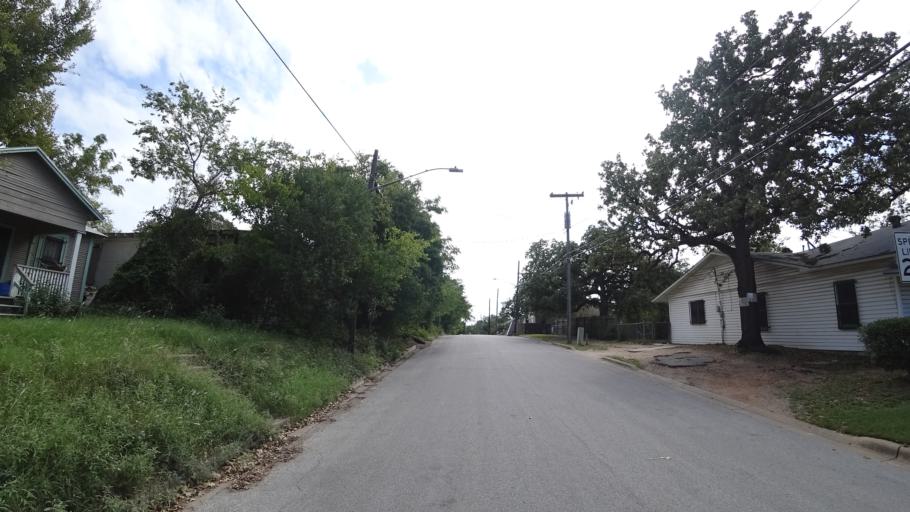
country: US
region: Texas
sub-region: Travis County
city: Austin
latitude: 30.2741
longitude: -97.7169
